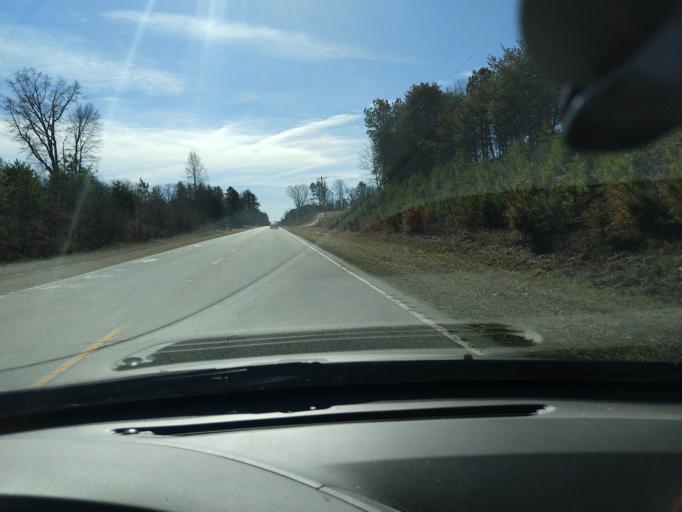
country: US
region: South Carolina
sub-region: Oconee County
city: Westminster
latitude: 34.6473
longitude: -83.1337
